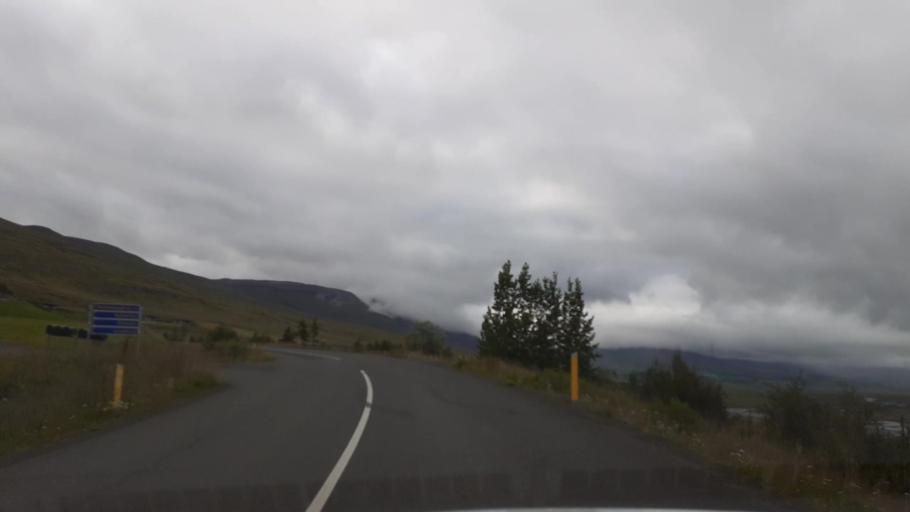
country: IS
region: Northeast
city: Akureyri
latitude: 65.6803
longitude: -18.0413
